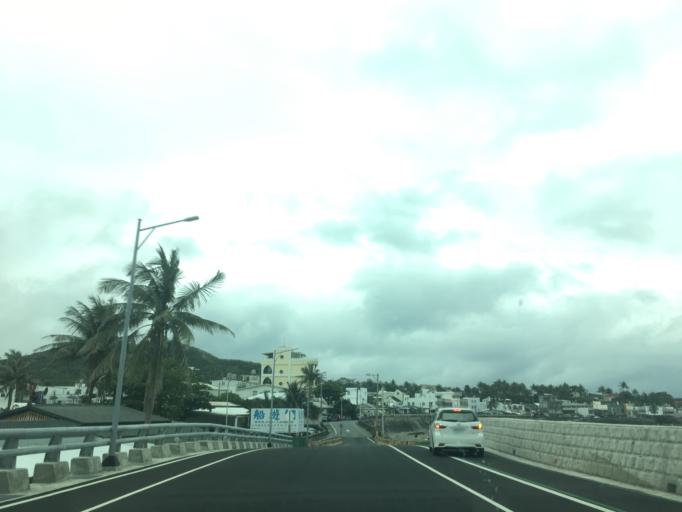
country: TW
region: Taiwan
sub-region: Taitung
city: Taitung
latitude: 22.7910
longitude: 121.1863
